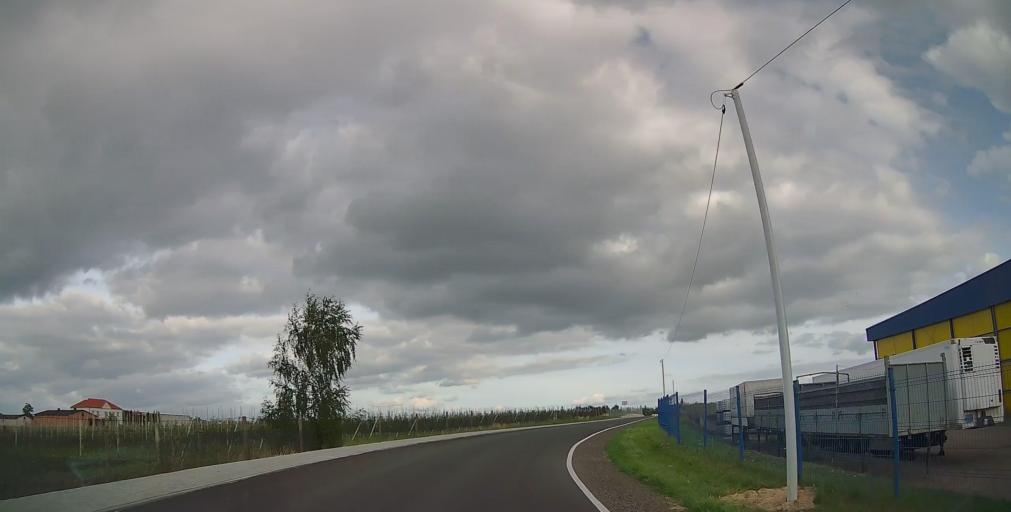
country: PL
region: Masovian Voivodeship
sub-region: Powiat bialobrzeski
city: Promna
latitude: 51.7089
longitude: 20.9536
